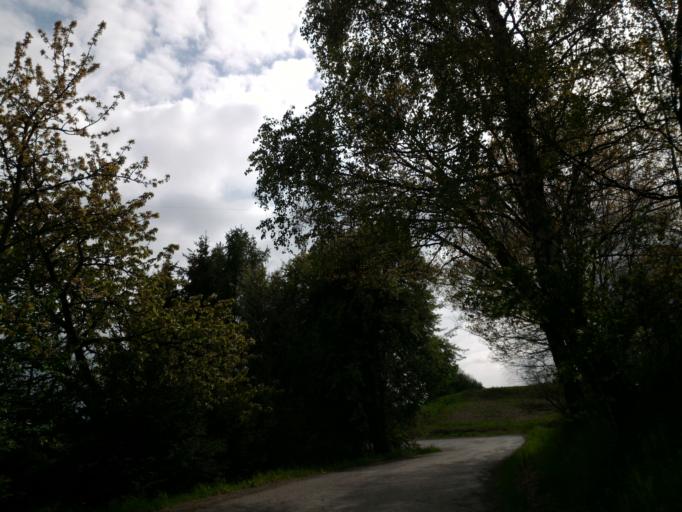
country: CZ
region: Vysocina
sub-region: Okres Havlickuv Brod
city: Svetla nad Sazavou
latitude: 49.6256
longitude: 15.3377
